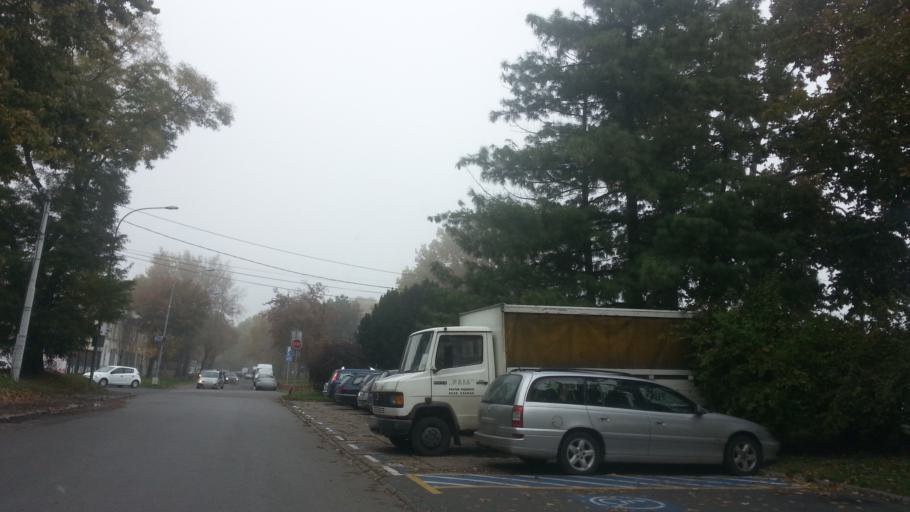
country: RS
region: Central Serbia
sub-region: Belgrade
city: Zemun
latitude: 44.8417
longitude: 20.4176
